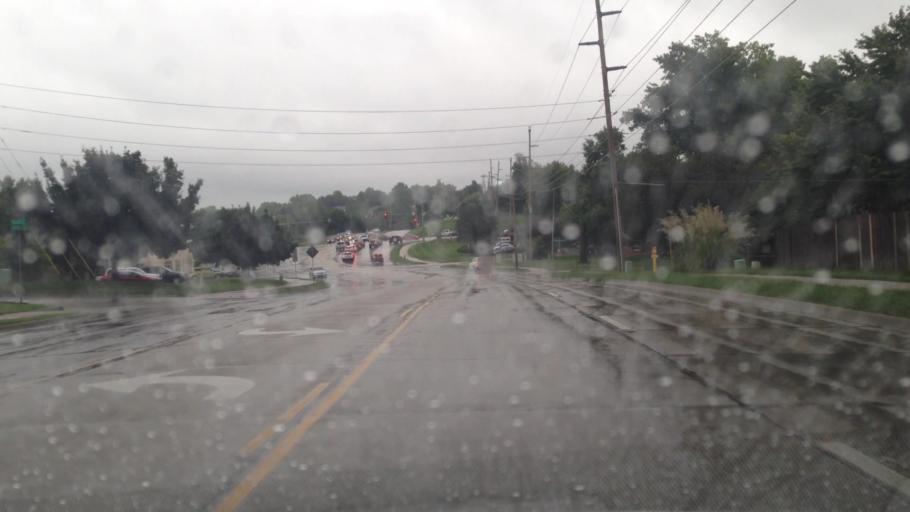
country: US
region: Kansas
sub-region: Douglas County
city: Lawrence
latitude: 38.9404
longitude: -95.2791
